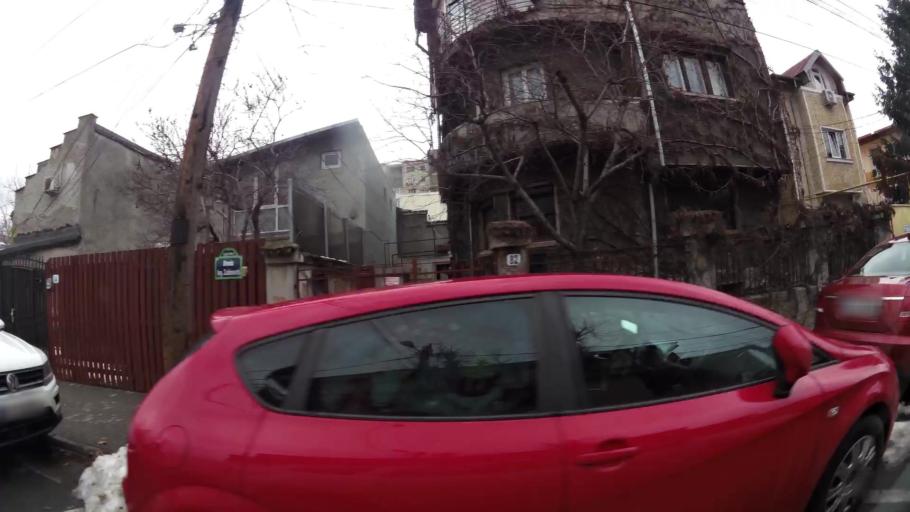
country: RO
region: Bucuresti
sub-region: Municipiul Bucuresti
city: Bucuresti
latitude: 44.4579
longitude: 26.0704
